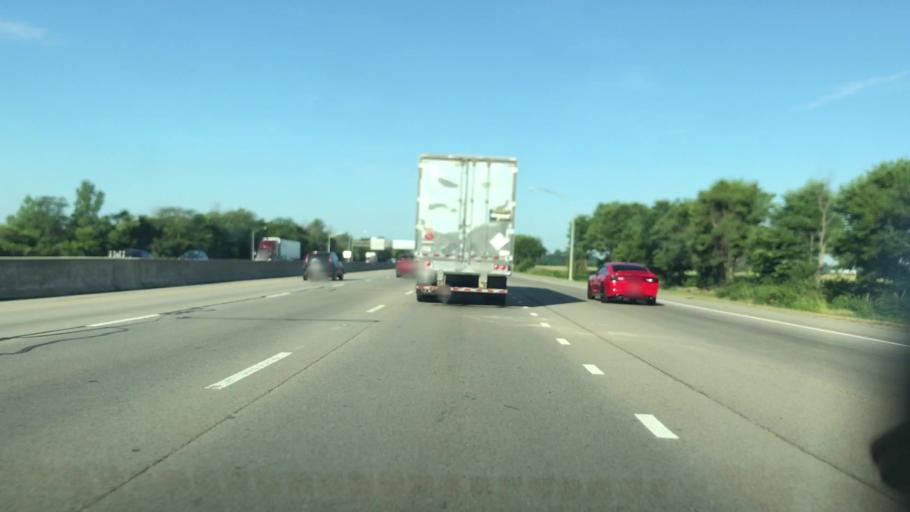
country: US
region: Ohio
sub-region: Clark County
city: Enon
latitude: 39.8827
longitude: -83.9502
